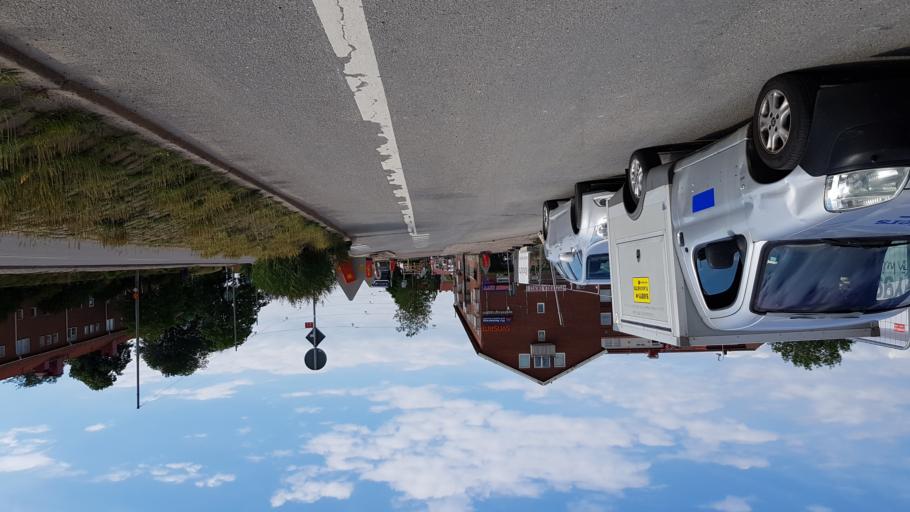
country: SE
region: Vaestra Goetaland
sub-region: Goteborg
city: Eriksbo
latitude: 57.7203
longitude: 12.0254
